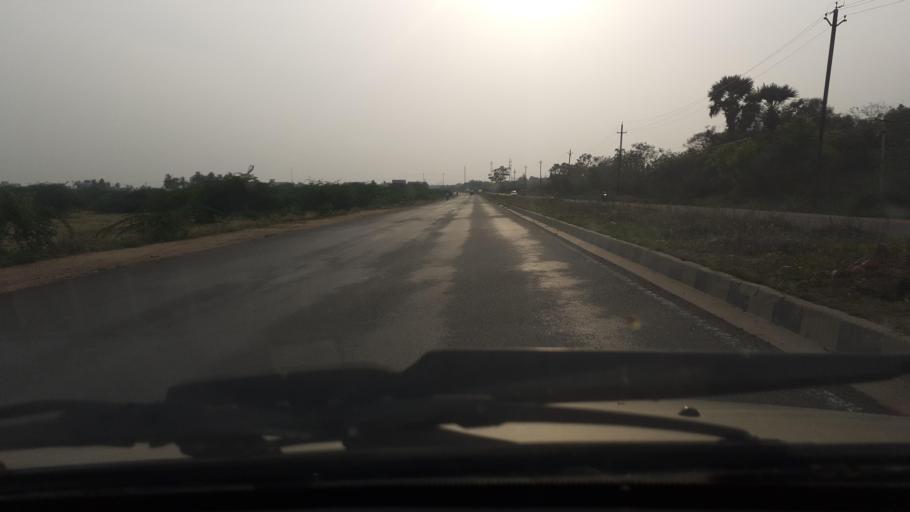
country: IN
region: Tamil Nadu
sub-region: Tirunelveli Kattabo
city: Tirunelveli
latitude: 8.7127
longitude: 77.7973
